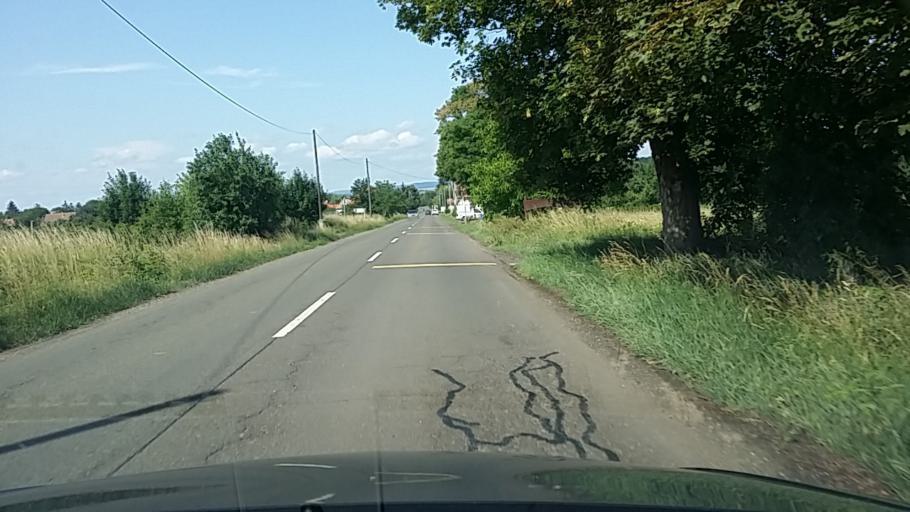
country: SK
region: Nitriansky
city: Sahy
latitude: 48.0372
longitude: 18.9086
